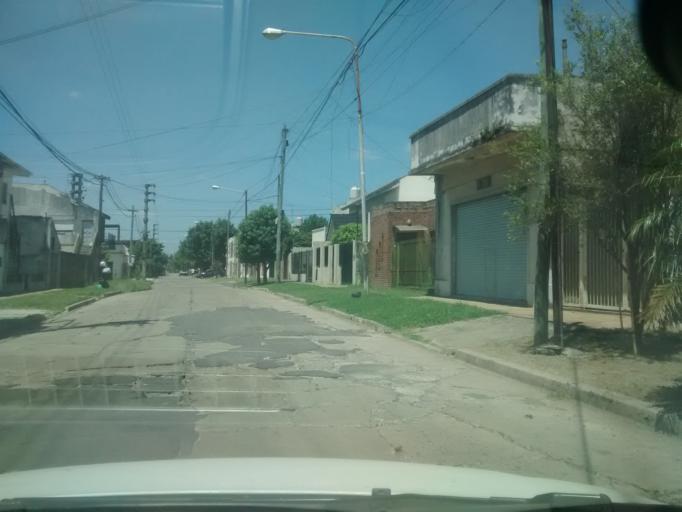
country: AR
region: Buenos Aires
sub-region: Partido de Moron
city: Moron
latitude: -34.6641
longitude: -58.6079
